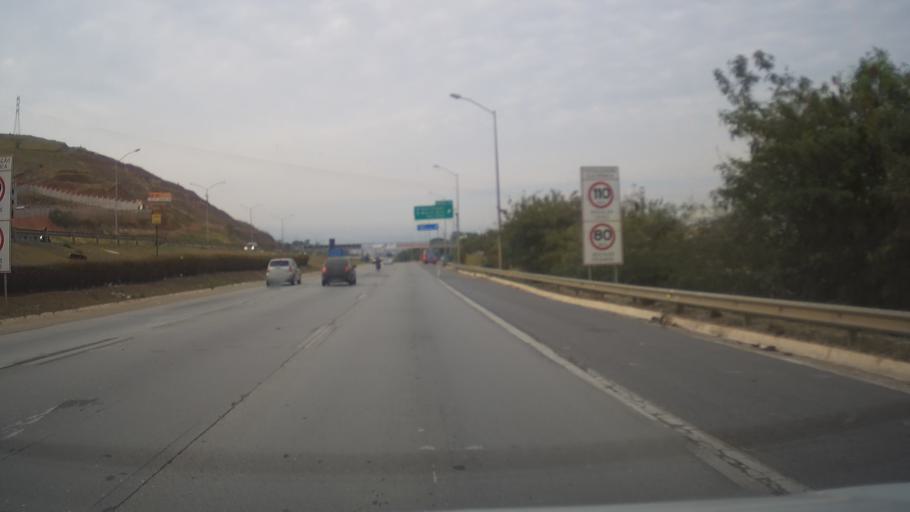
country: BR
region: Minas Gerais
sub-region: Vespasiano
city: Vespasiano
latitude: -19.7735
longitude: -43.9488
